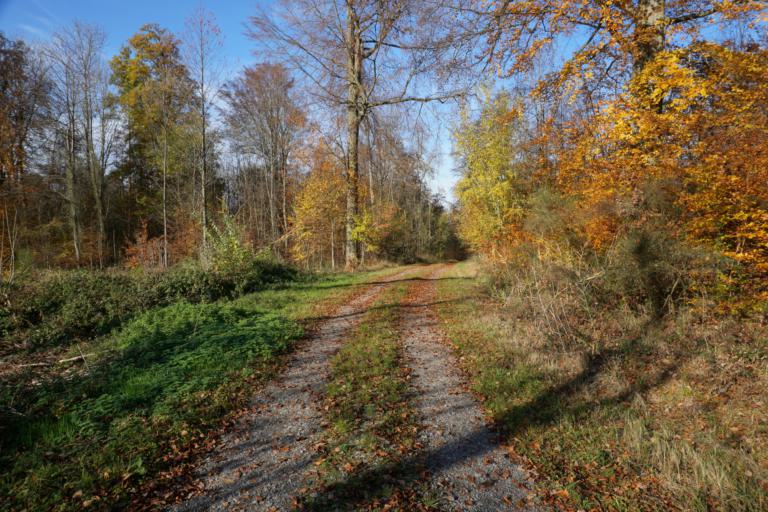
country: DE
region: Baden-Wuerttemberg
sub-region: Karlsruhe Region
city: Aglasterhausen
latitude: 49.3652
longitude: 8.9978
